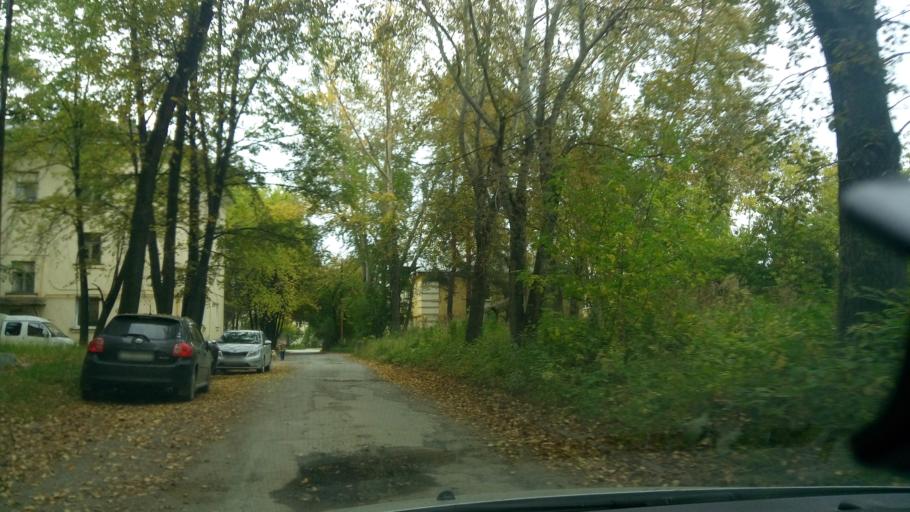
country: RU
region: Sverdlovsk
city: Sovkhoznyy
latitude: 56.7790
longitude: 60.5924
